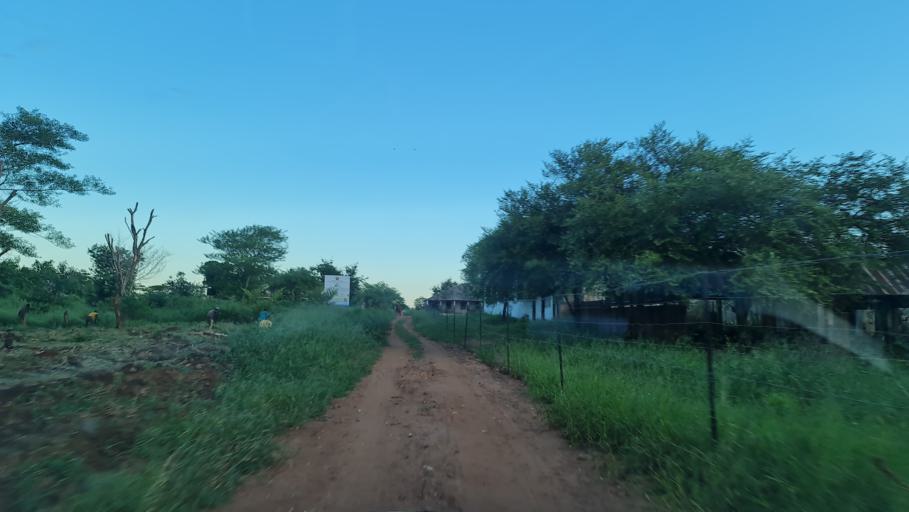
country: MZ
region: Nampula
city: Ilha de Mocambique
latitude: -14.9866
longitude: 40.0950
